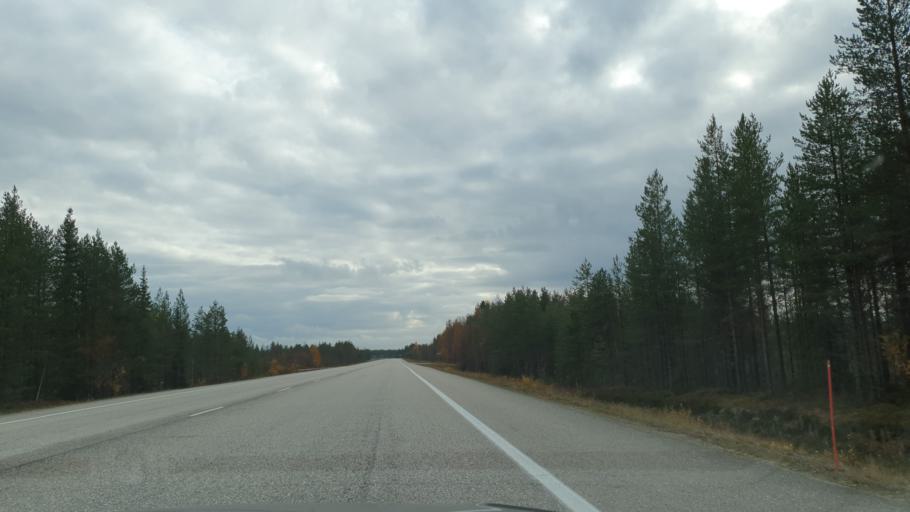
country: FI
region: Northern Ostrobothnia
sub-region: Oulunkaari
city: Pudasjaervi
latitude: 65.4074
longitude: 26.8968
